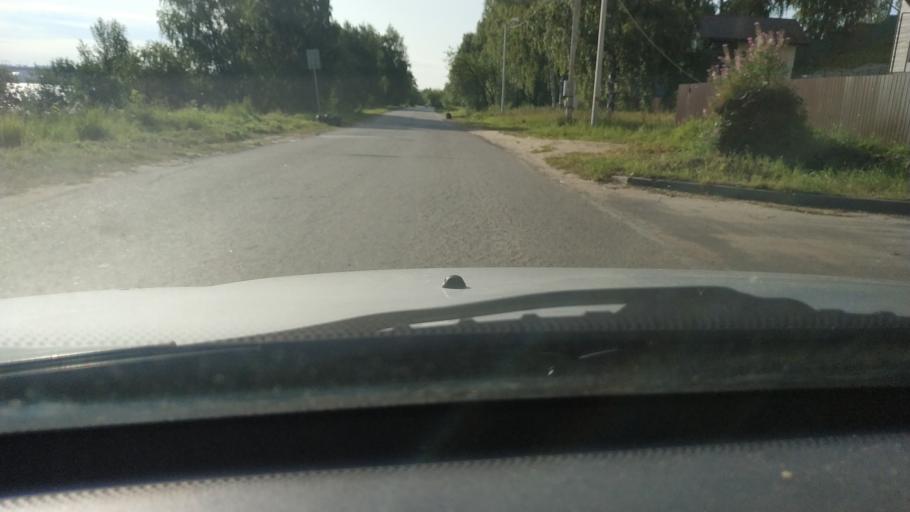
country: RU
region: Kostroma
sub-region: Kostromskoy Rayon
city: Kostroma
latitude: 57.7541
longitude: 40.9211
